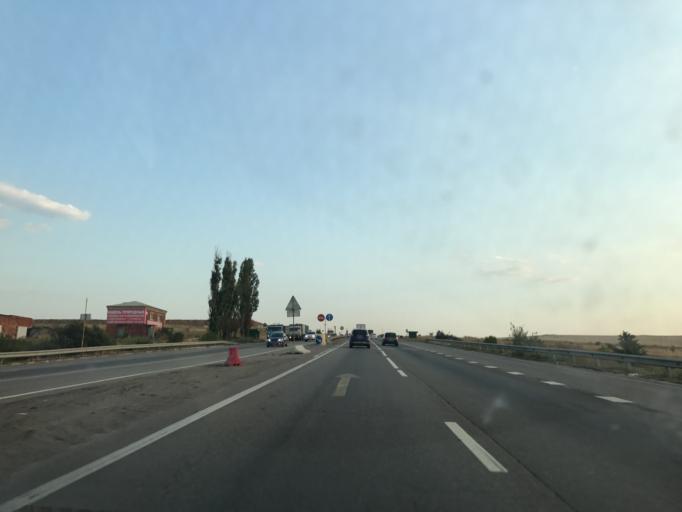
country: RU
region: Rostov
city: Likhoy
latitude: 48.1364
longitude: 40.2596
